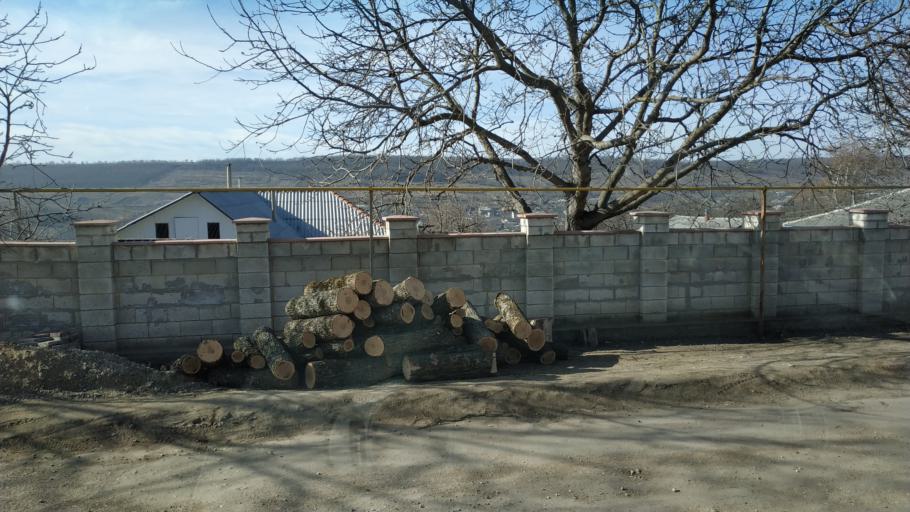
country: MD
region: Chisinau
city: Vatra
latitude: 47.0289
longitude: 28.6362
